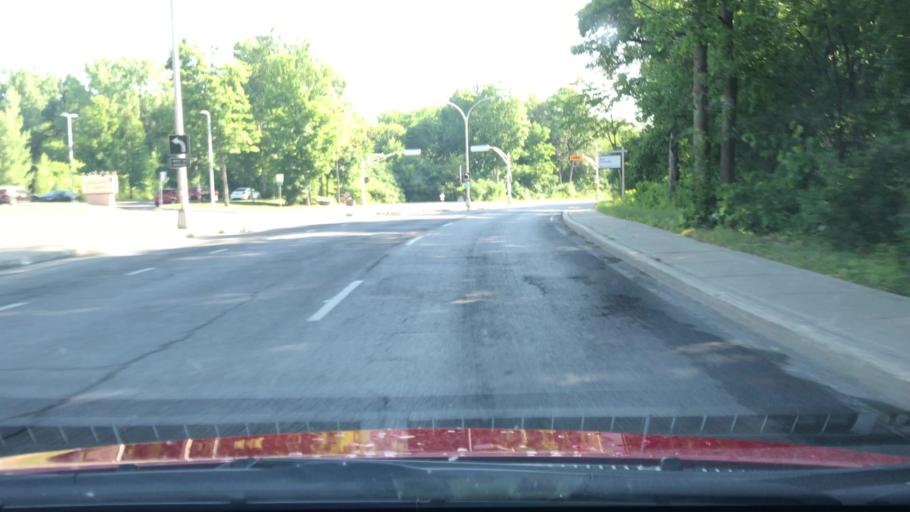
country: CA
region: Quebec
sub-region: Laval
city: Laval
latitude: 45.5480
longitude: -73.7337
